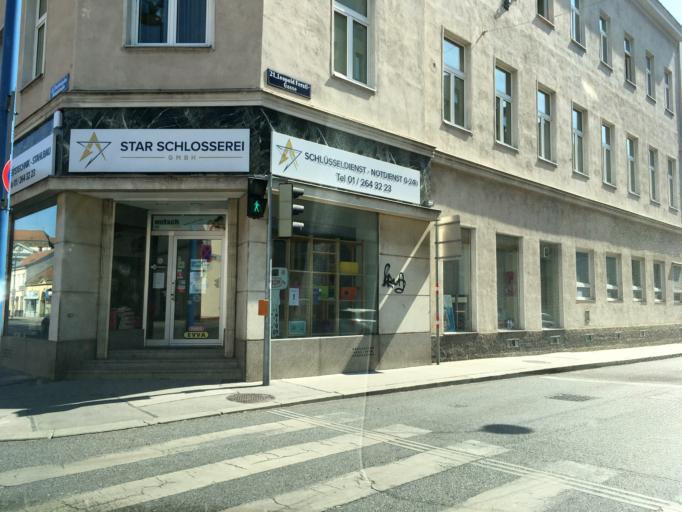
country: AT
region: Vienna
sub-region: Wien Stadt
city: Vienna
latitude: 48.2558
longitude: 16.3964
